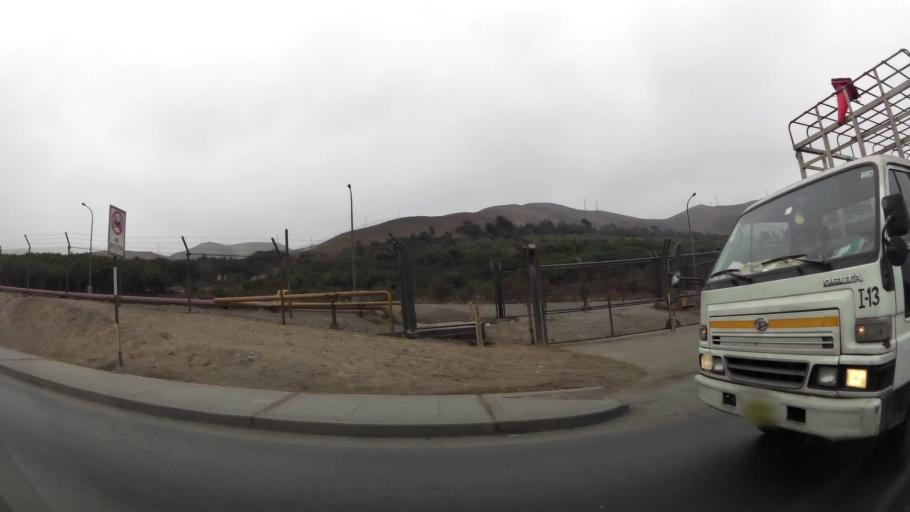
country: PE
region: Lima
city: Ventanilla
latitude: -11.9187
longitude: -77.1286
